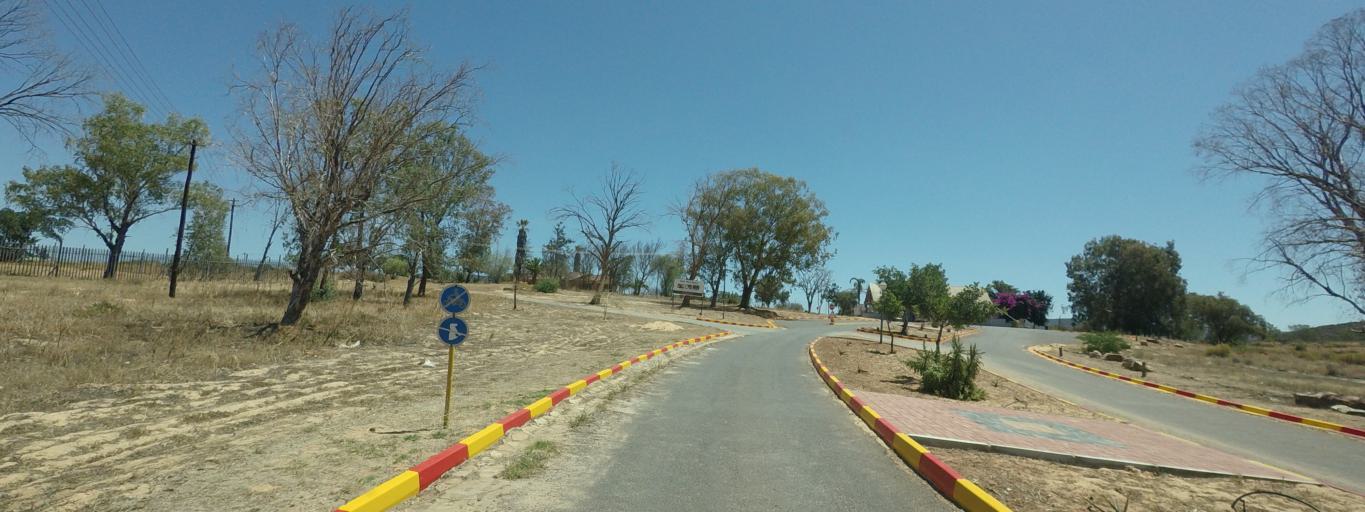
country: ZA
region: Western Cape
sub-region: West Coast District Municipality
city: Clanwilliam
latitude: -32.1902
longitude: 18.8874
